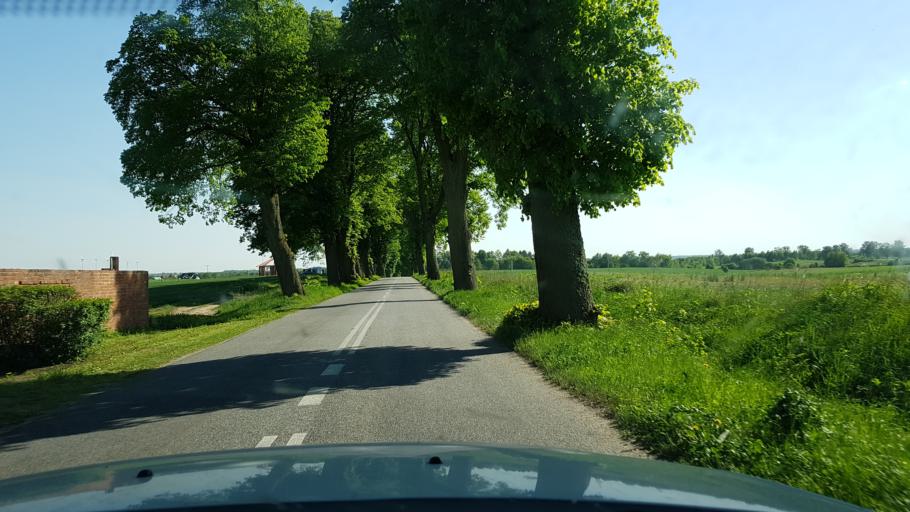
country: PL
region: West Pomeranian Voivodeship
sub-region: Powiat lobeski
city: Resko
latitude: 53.7855
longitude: 15.4105
